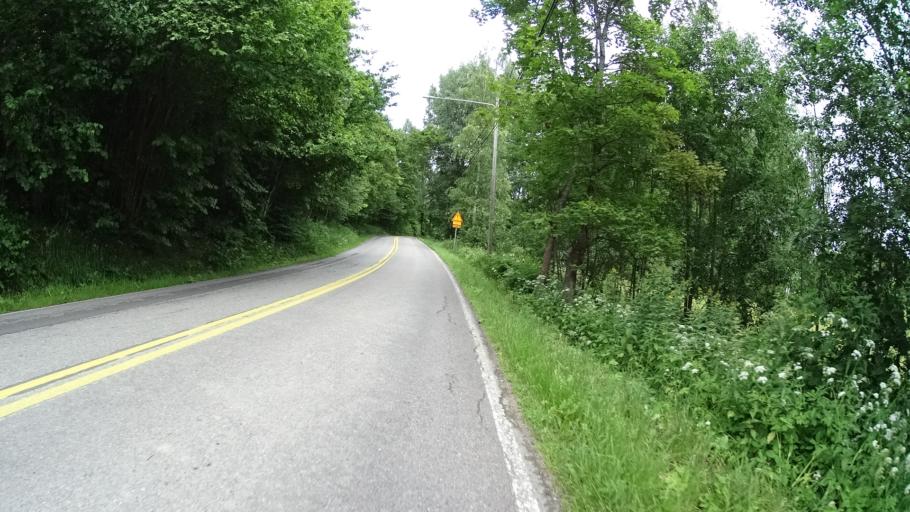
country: FI
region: Uusimaa
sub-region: Helsinki
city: Espoo
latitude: 60.2675
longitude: 24.6546
